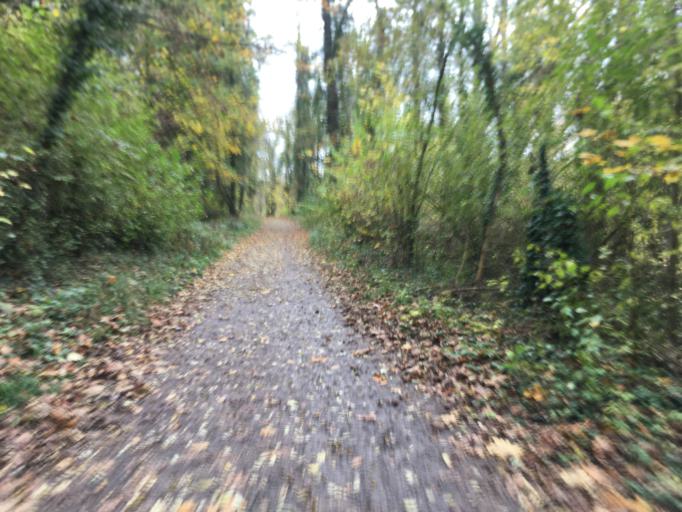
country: DE
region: Baden-Wuerttemberg
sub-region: Freiburg Region
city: Sasbach
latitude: 48.1116
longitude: 7.5860
